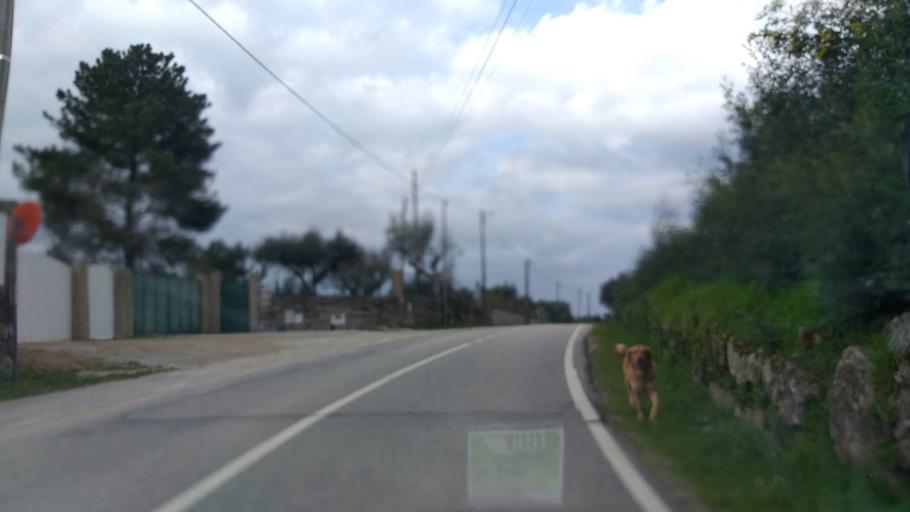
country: PT
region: Guarda
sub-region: Seia
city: Seia
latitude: 40.4885
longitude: -7.6326
